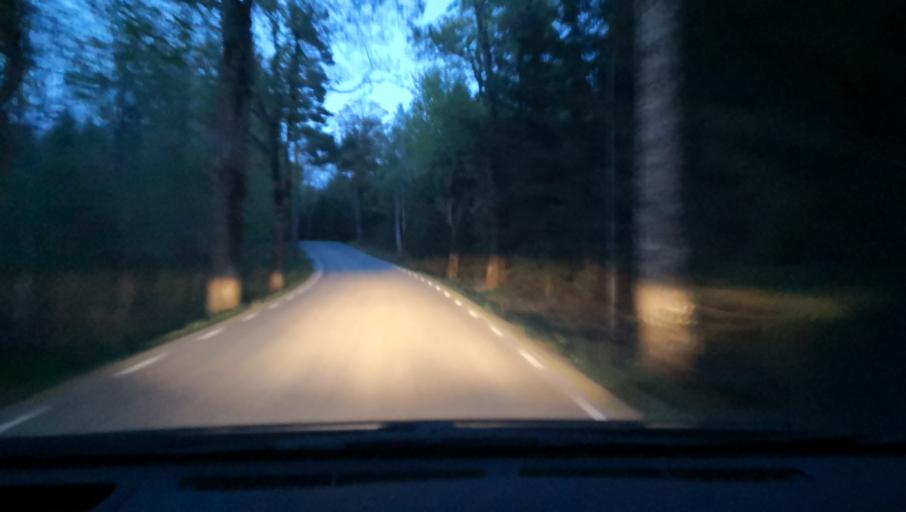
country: SE
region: OErebro
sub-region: Orebro Kommun
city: Vintrosa
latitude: 59.1713
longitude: 15.0115
